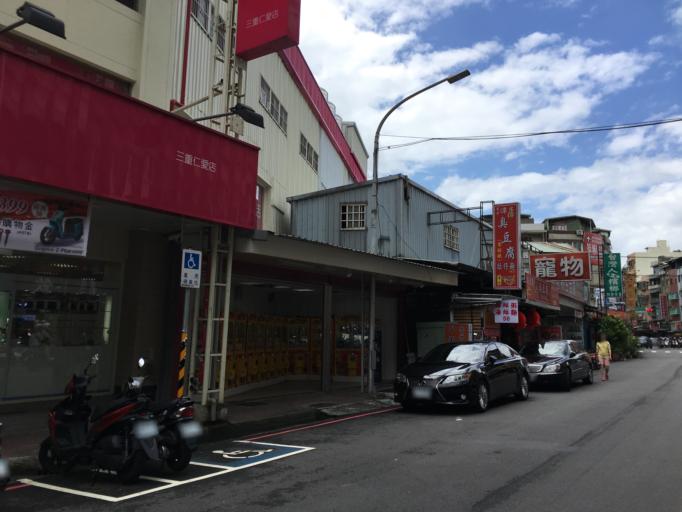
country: TW
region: Taipei
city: Taipei
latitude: 25.0823
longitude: 121.4885
